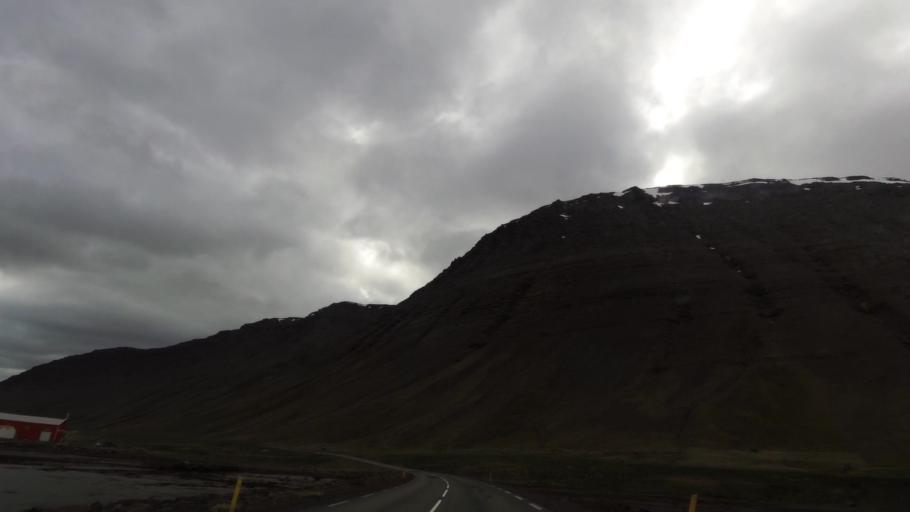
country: IS
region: Westfjords
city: Isafjoerdur
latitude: 66.0528
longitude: -23.1495
